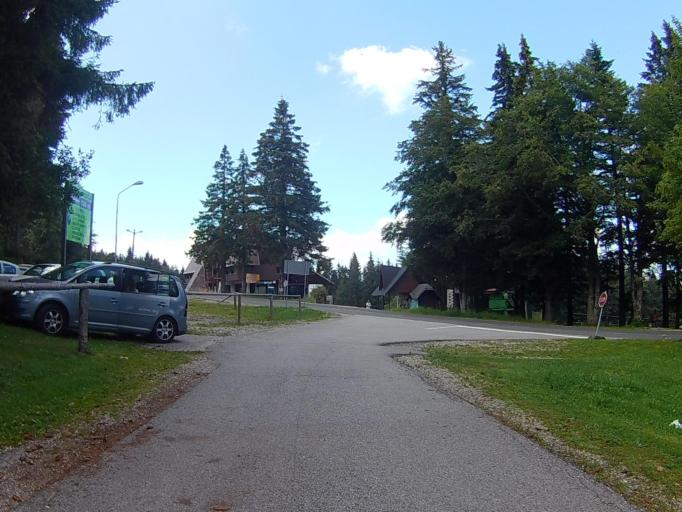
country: SI
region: Ruse
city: Ruse
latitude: 46.4956
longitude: 15.5080
